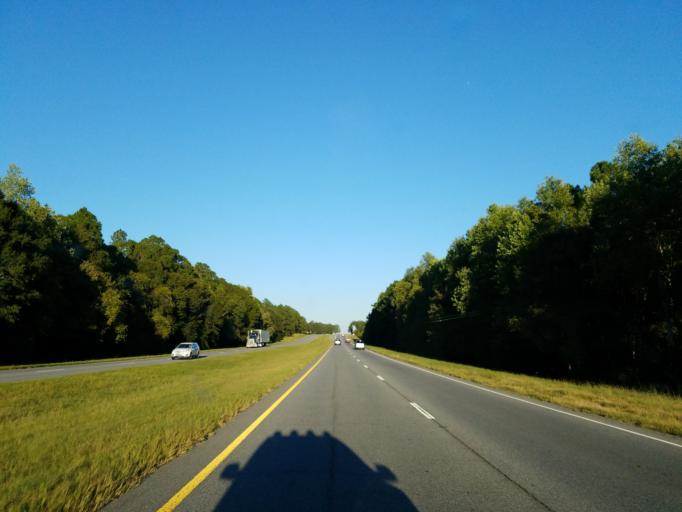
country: US
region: Georgia
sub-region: Worth County
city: Sylvester
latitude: 31.5101
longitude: -83.7658
